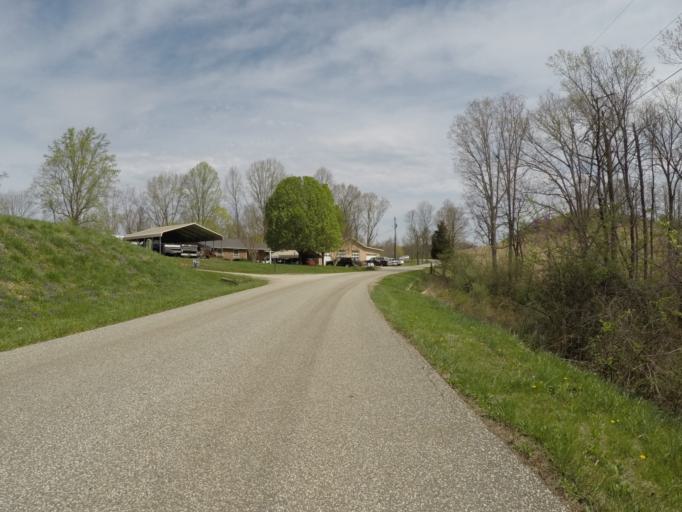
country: US
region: West Virginia
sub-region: Wayne County
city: Lavalette
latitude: 38.3332
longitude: -82.3638
